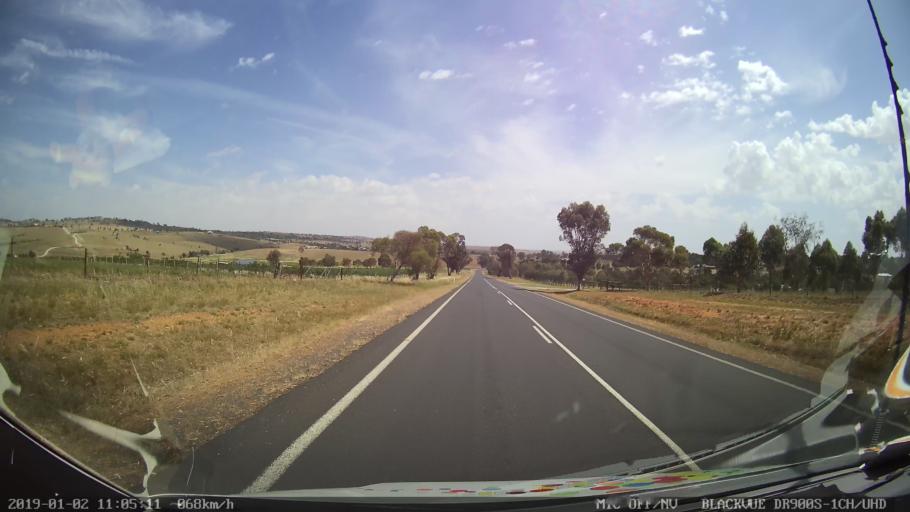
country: AU
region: New South Wales
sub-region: Young
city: Young
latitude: -34.5677
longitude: 148.3541
